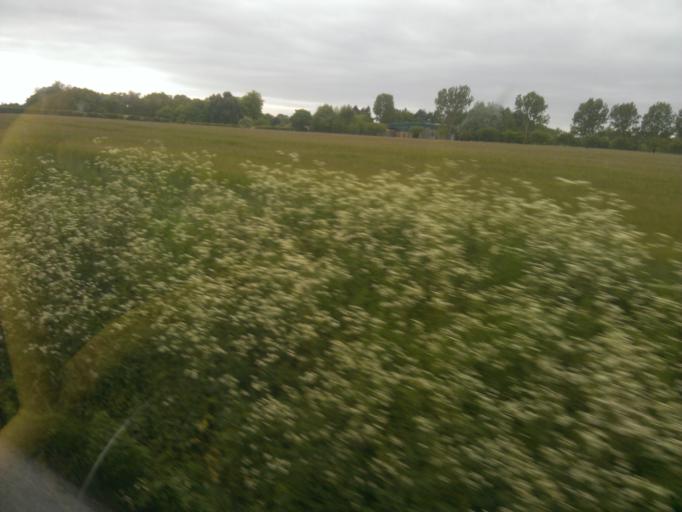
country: GB
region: England
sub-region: Suffolk
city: East Bergholt
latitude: 51.9584
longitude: 0.9637
